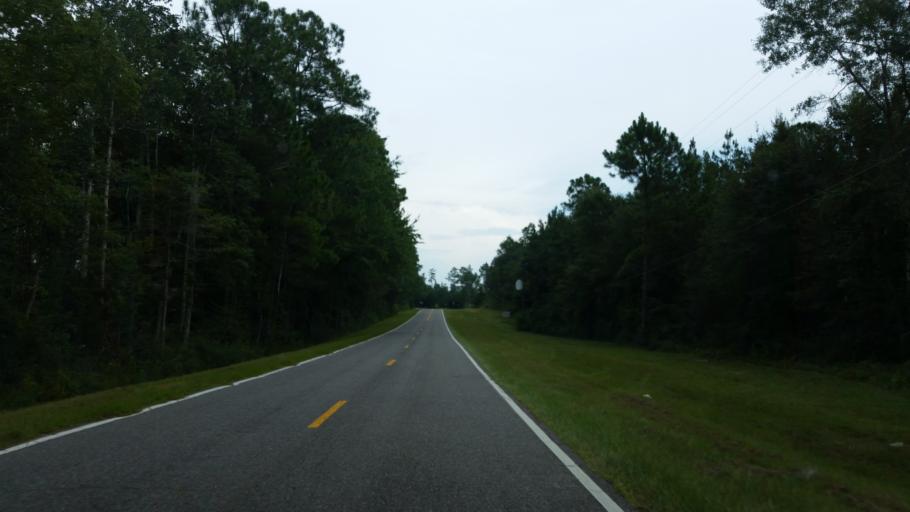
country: US
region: Florida
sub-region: Escambia County
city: Molino
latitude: 30.6787
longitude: -87.3232
